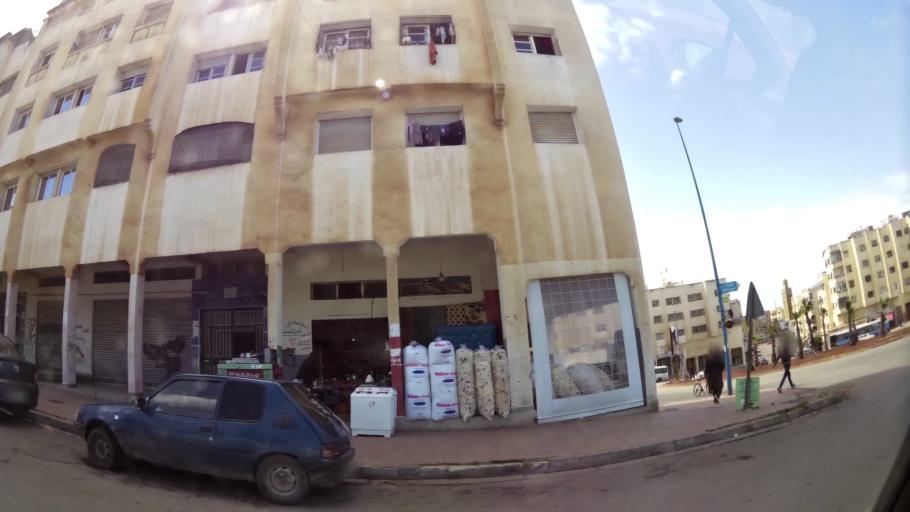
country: MA
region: Grand Casablanca
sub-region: Mediouna
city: Tit Mellil
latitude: 33.6039
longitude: -7.4816
